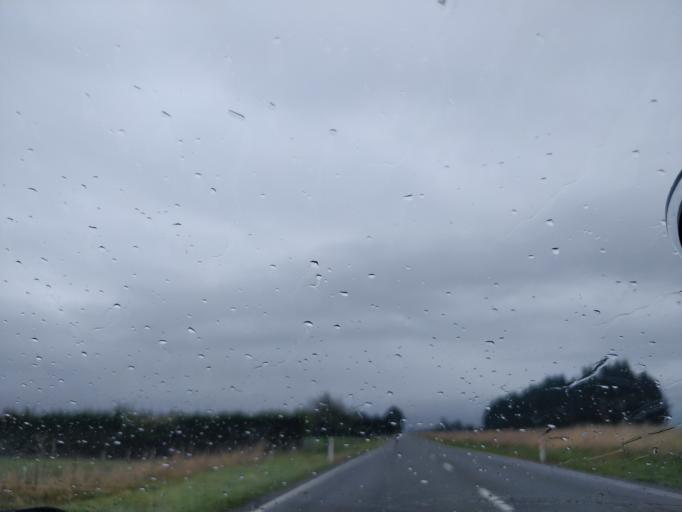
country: NZ
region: Canterbury
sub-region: Selwyn District
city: Darfield
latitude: -43.3809
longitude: 172.0055
